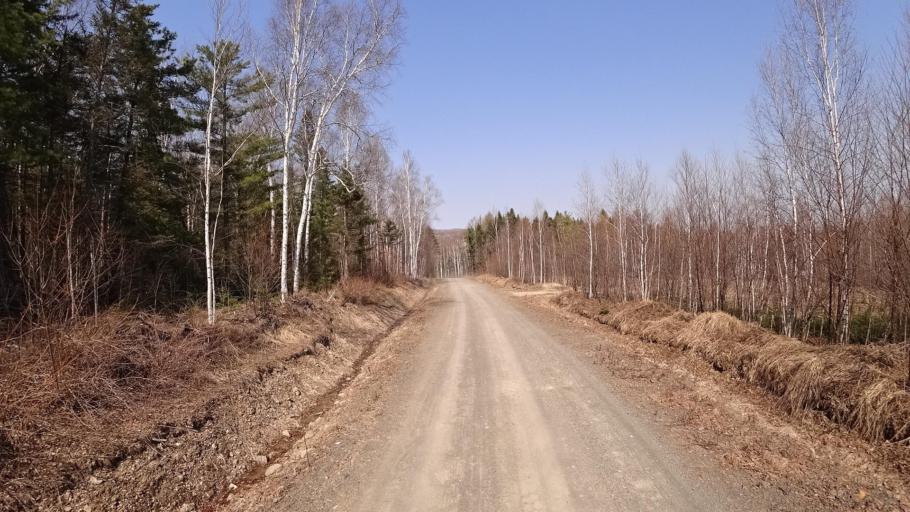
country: RU
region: Khabarovsk Krai
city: Selikhino
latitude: 50.6322
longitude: 137.4072
